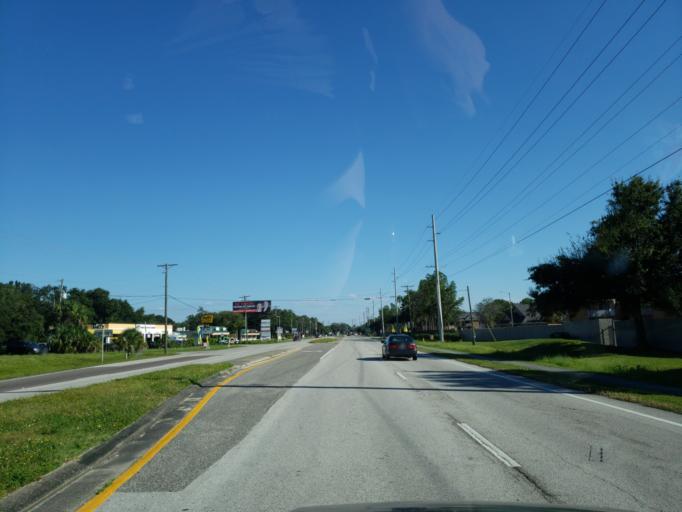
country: US
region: Florida
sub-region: Hillsborough County
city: Carrollwood Village
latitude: 28.0462
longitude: -82.5163
